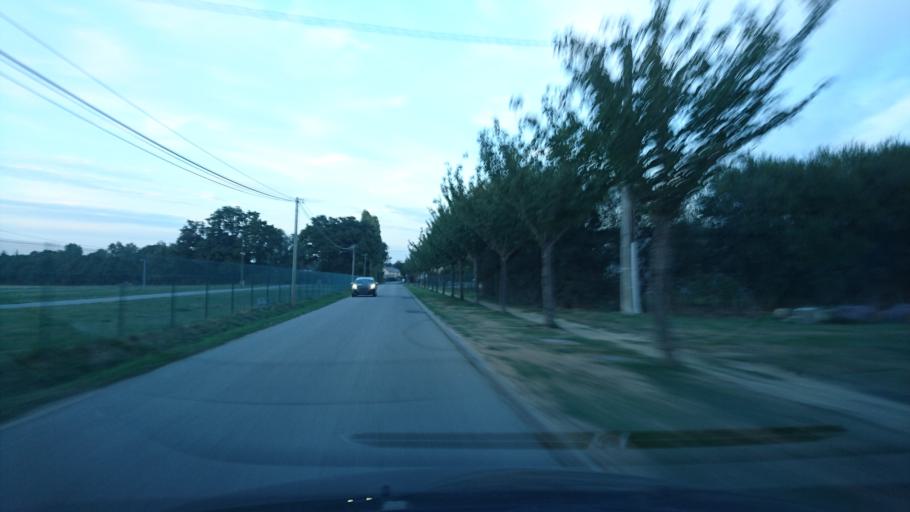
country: FR
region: Brittany
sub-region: Departement d'Ille-et-Vilaine
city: Guipry
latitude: 47.8634
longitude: -1.8914
